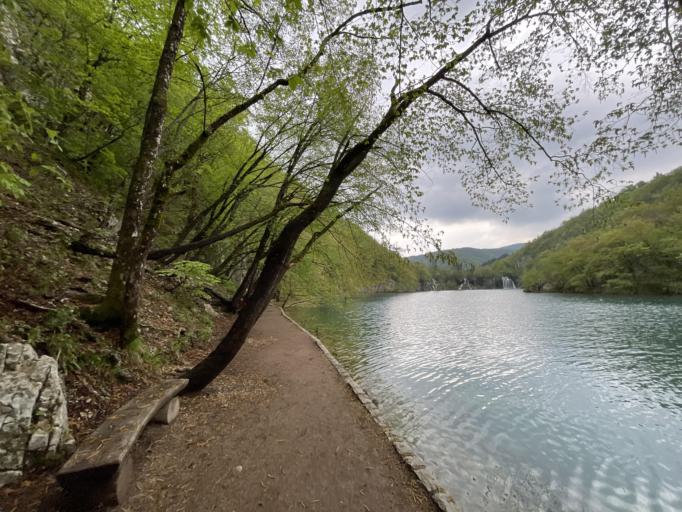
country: HR
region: Licko-Senjska
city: Jezerce
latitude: 44.8963
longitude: 15.6111
